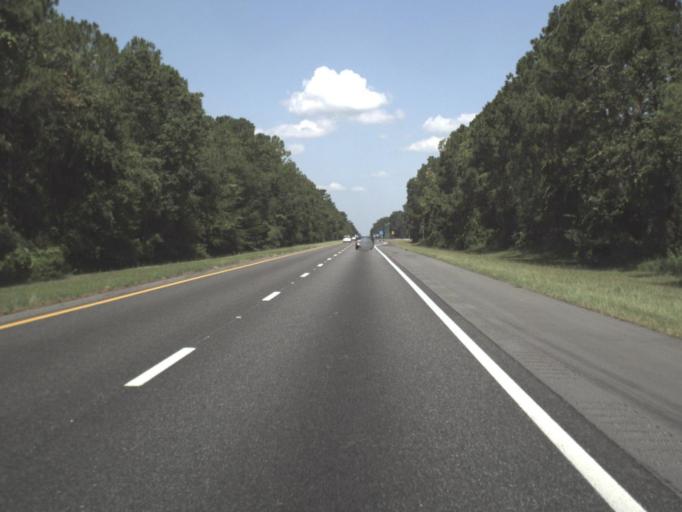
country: US
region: Florida
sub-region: Madison County
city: Madison
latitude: 30.3663
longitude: -83.2370
